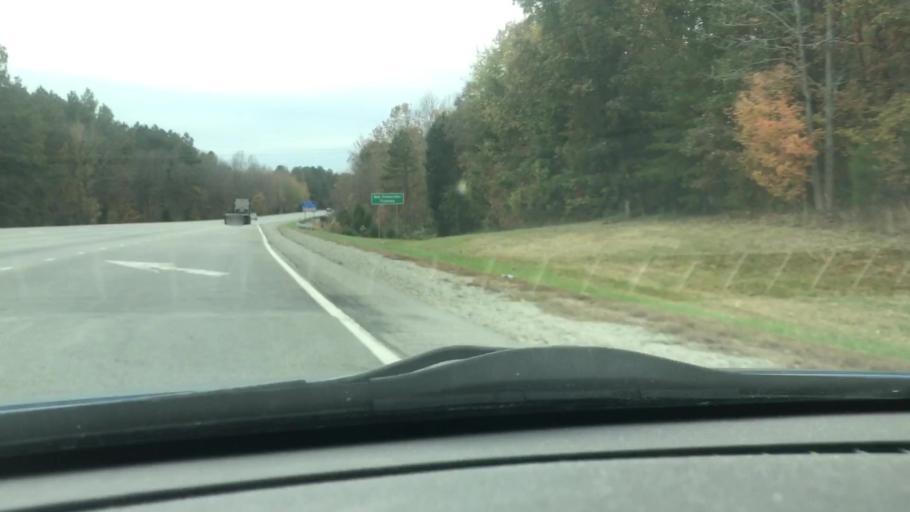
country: US
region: North Carolina
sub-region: Davidson County
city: Lexington
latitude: 35.8065
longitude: -80.1864
